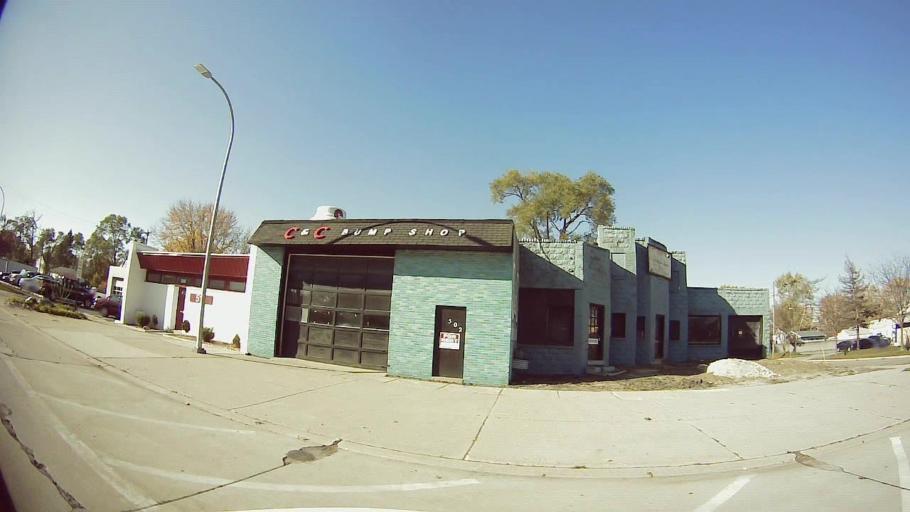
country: US
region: Michigan
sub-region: Oakland County
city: Clawson
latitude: 42.5295
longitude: -83.1460
